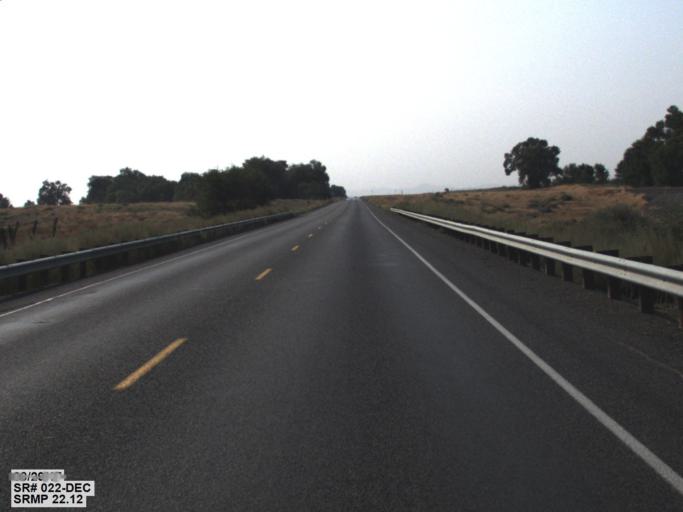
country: US
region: Washington
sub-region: Yakima County
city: Mabton
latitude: 46.2164
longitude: -120.0192
